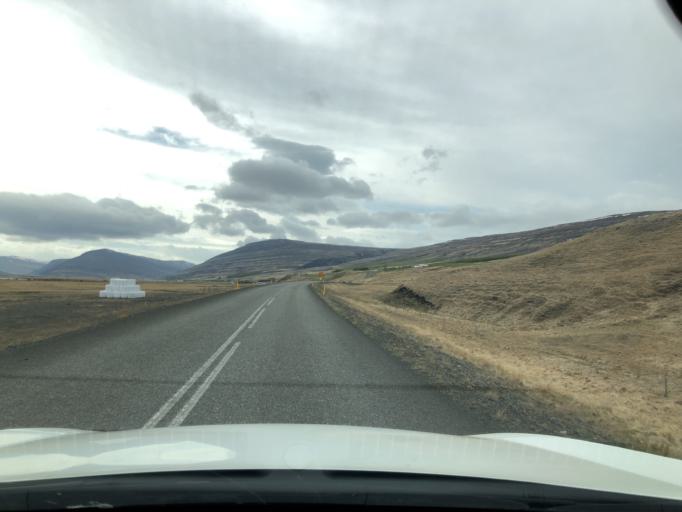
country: IS
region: East
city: Egilsstadir
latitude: 65.0753
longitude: -14.8720
